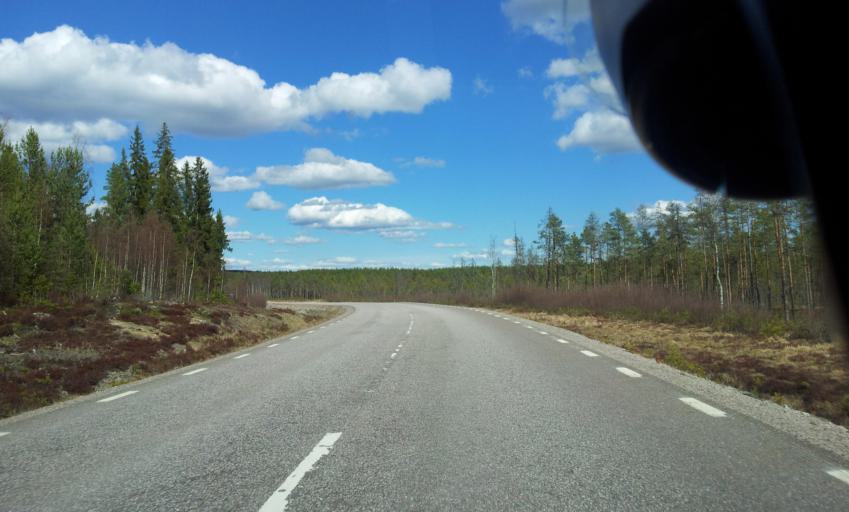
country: SE
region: Gaevleborg
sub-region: Ovanakers Kommun
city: Edsbyn
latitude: 61.2802
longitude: 15.9005
